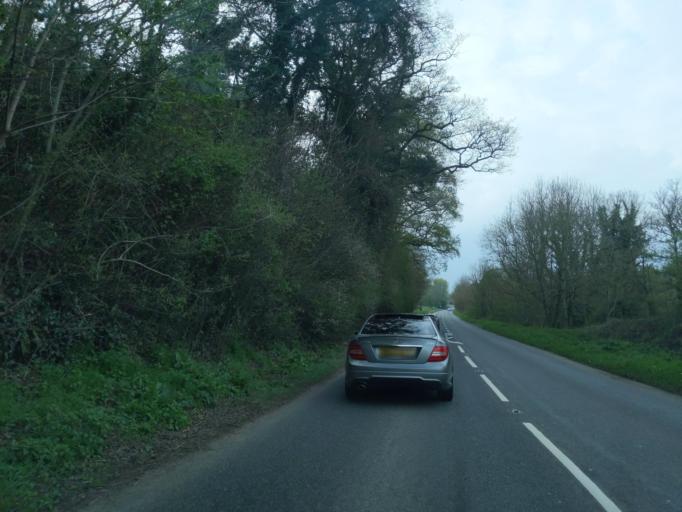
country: GB
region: England
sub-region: Devon
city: Exeter
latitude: 50.7605
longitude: -3.5616
